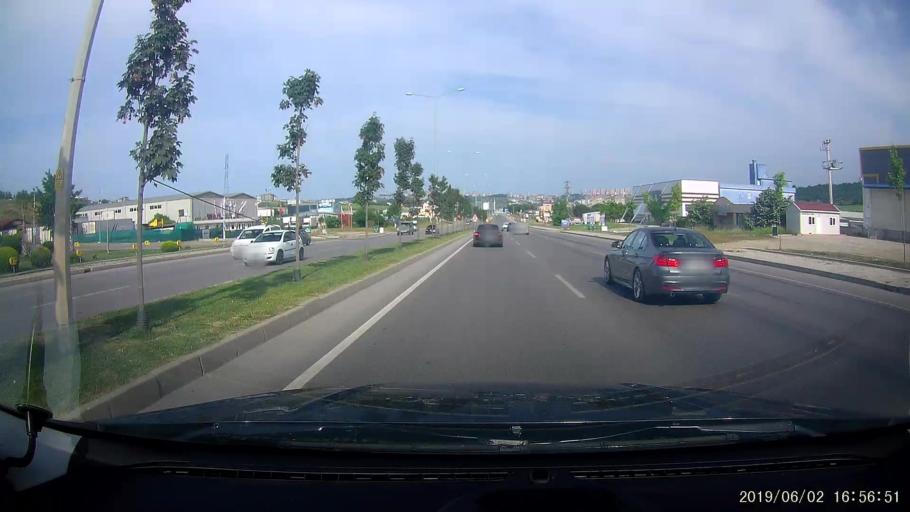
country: TR
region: Samsun
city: Samsun
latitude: 41.2919
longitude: 36.2663
